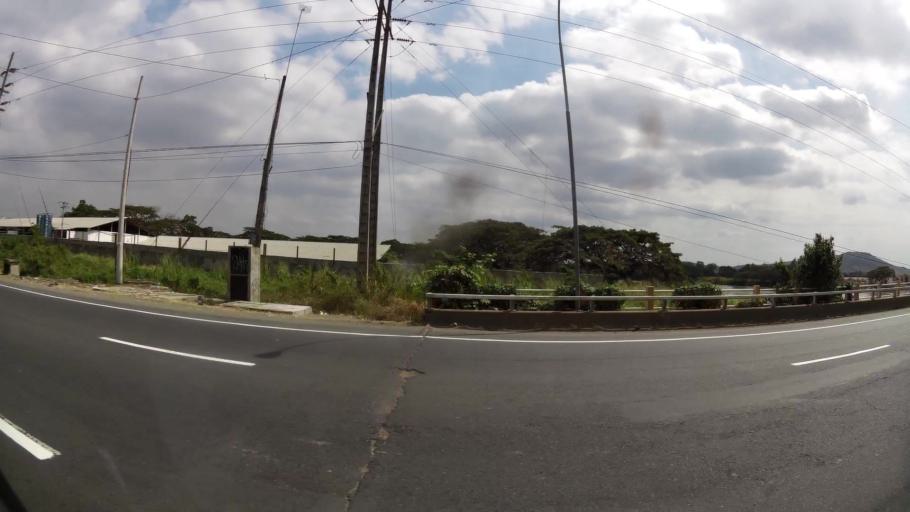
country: EC
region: Guayas
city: Eloy Alfaro
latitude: -2.0641
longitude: -79.9253
